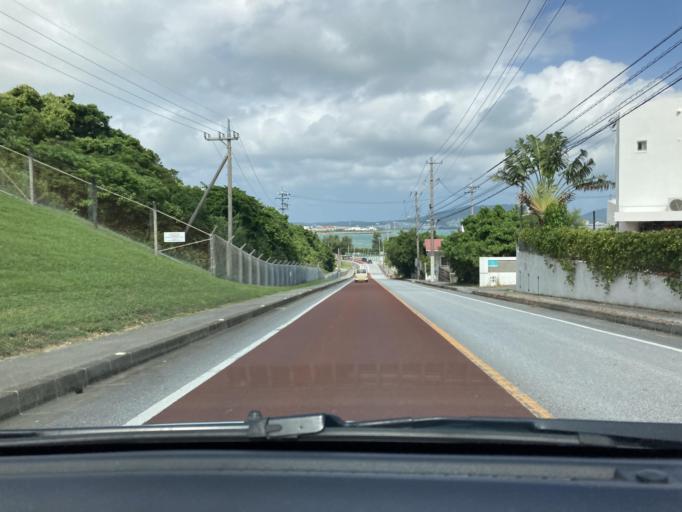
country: JP
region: Okinawa
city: Ishikawa
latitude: 26.4029
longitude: 127.8452
